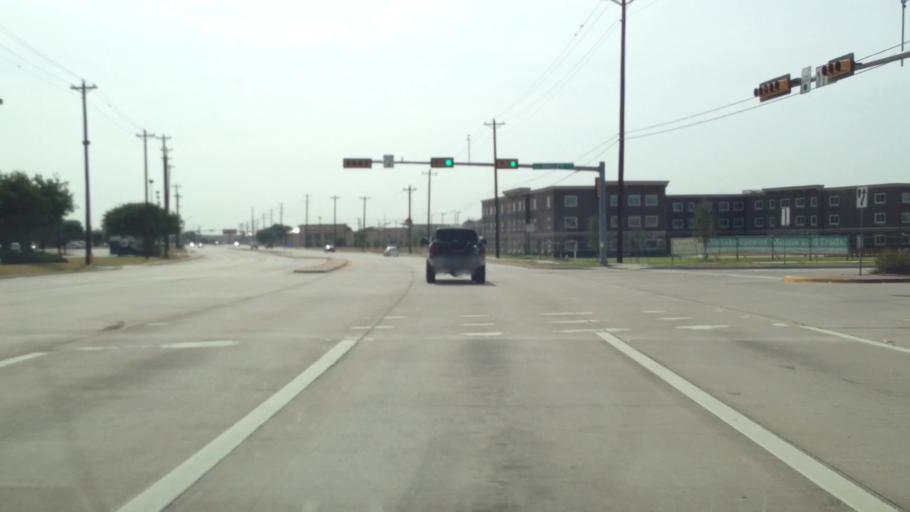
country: US
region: Texas
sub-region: Denton County
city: Lewisville
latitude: 33.0061
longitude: -97.0196
